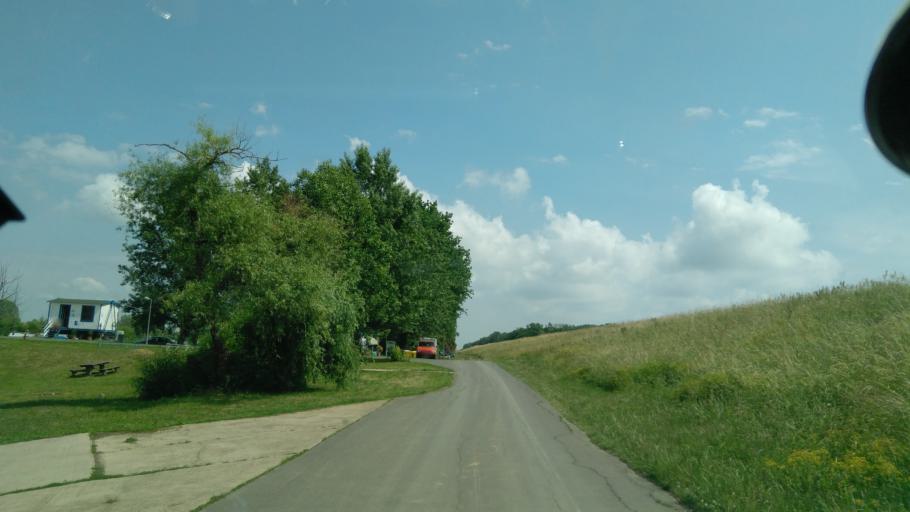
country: HU
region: Bekes
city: Bekes
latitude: 46.7608
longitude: 21.1536
